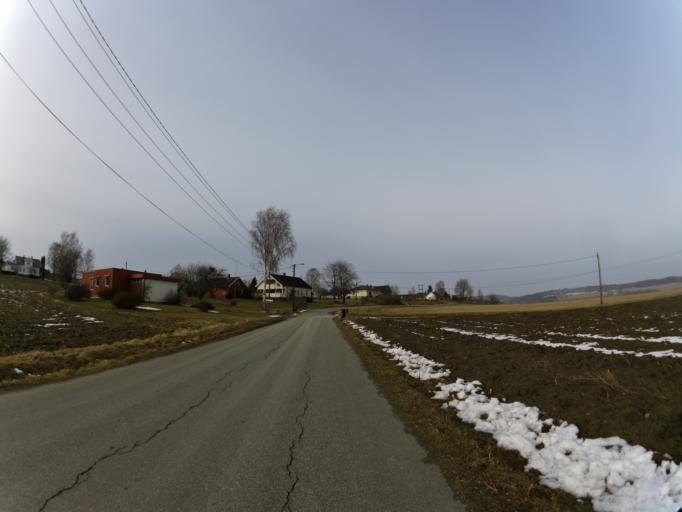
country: NO
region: Ostfold
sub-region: Fredrikstad
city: Fredrikstad
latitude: 59.2798
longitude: 11.0000
